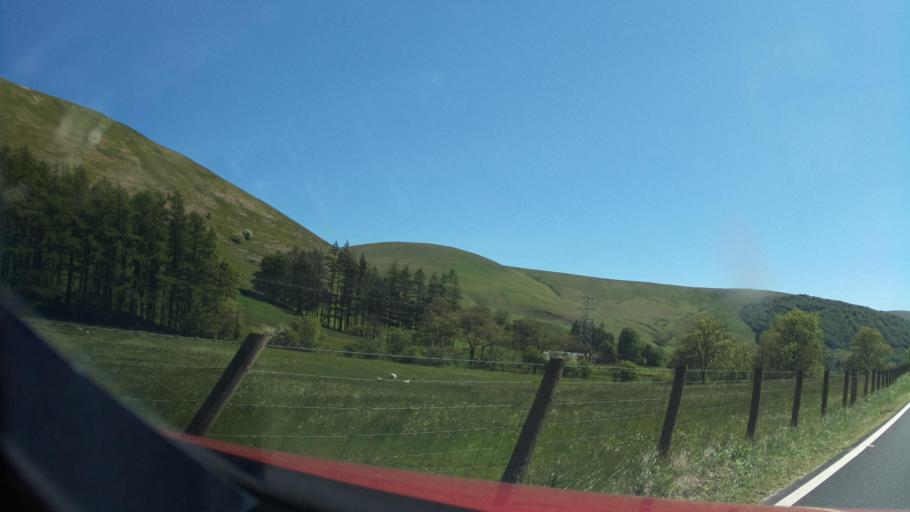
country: GB
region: Scotland
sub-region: Dumfries and Galloway
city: Langholm
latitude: 55.2619
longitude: -2.9666
